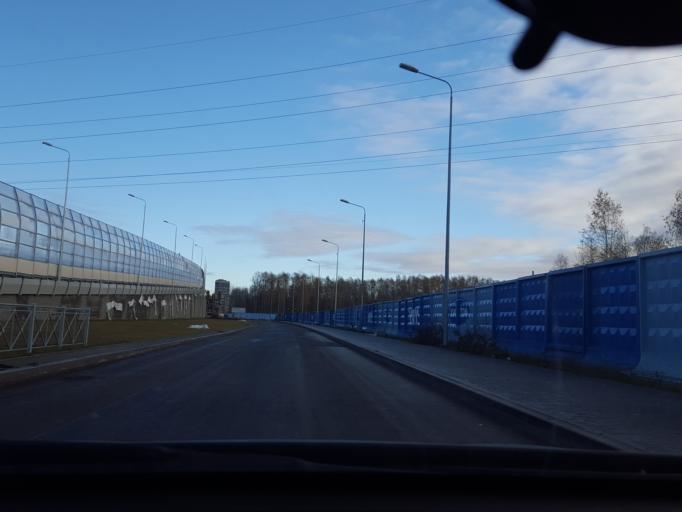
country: RU
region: St.-Petersburg
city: Shuvalovo
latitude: 60.0600
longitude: 30.2772
